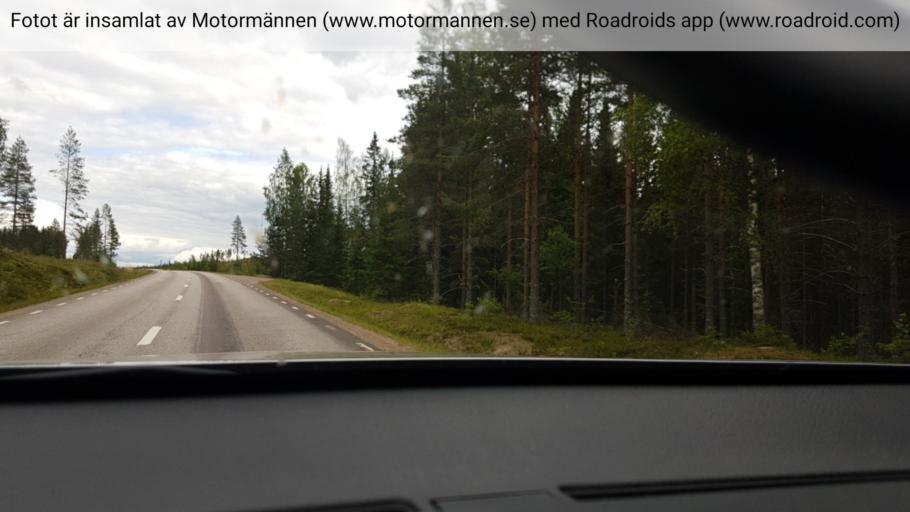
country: NO
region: Hedmark
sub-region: Trysil
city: Innbygda
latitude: 61.0259
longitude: 12.4911
